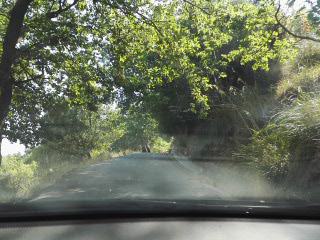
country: IT
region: Calabria
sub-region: Provincia di Reggio Calabria
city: Stilo
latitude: 38.4534
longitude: 16.4620
